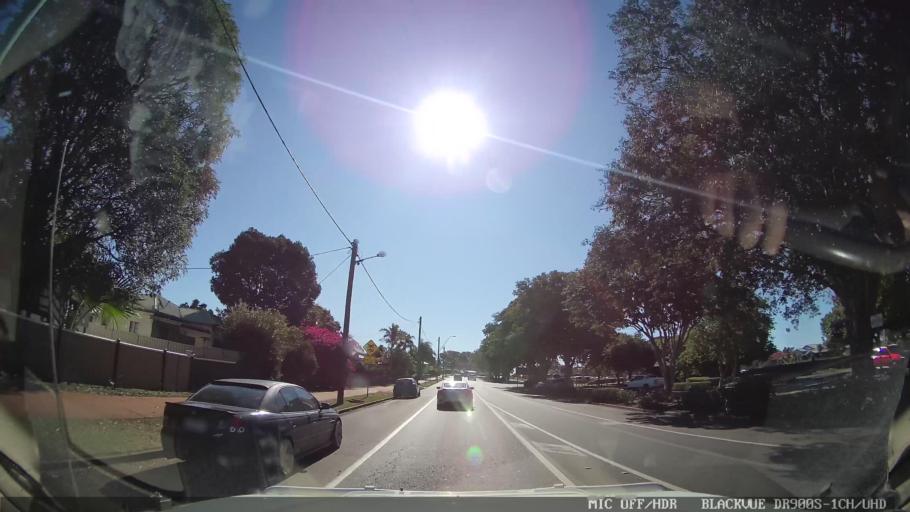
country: AU
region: Queensland
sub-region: Bundaberg
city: Childers
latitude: -25.2351
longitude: 152.2744
